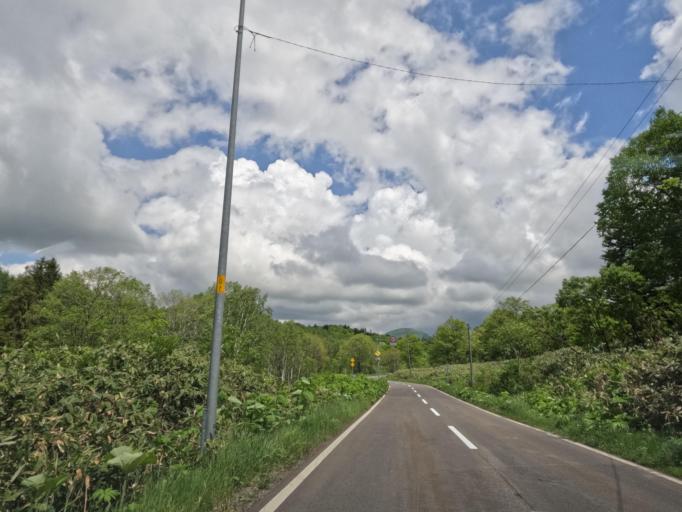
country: JP
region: Hokkaido
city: Takikawa
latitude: 43.5429
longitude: 141.6387
